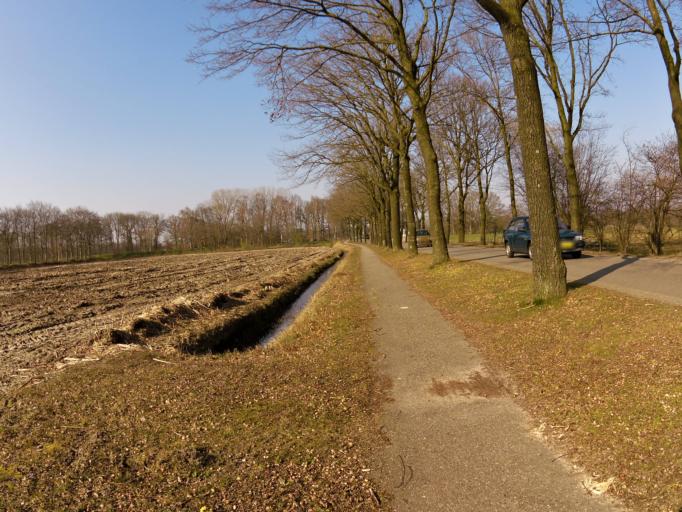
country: NL
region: North Brabant
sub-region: Gemeente Sint-Michielsgestel
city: Sint-Michielsgestel
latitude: 51.6992
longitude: 5.3858
